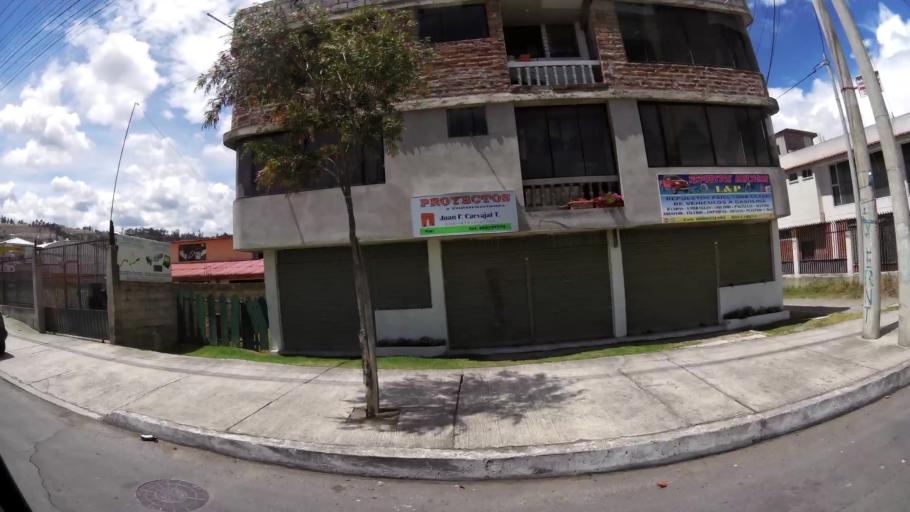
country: EC
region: Tungurahua
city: Ambato
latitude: -1.2785
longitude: -78.6336
